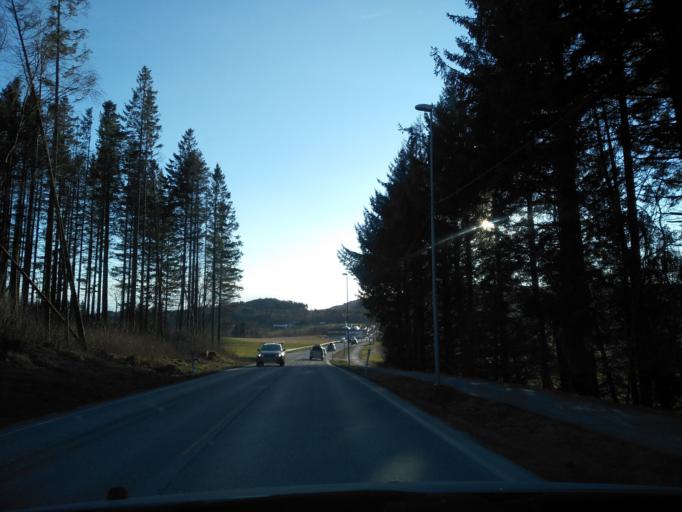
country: NO
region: Rogaland
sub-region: Tysvaer
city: Aksdal
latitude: 59.4846
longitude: 5.5410
